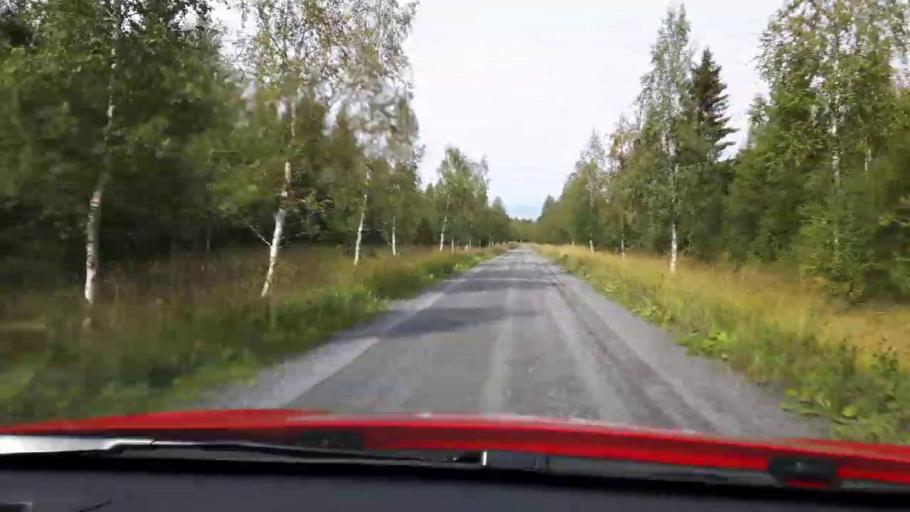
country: SE
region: Jaemtland
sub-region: Krokoms Kommun
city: Valla
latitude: 63.2614
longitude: 13.8000
